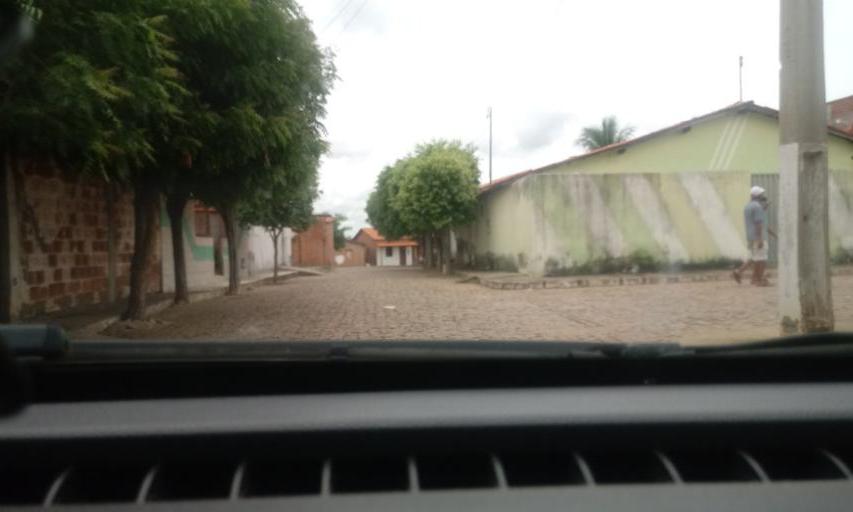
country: BR
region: Bahia
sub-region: Riacho De Santana
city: Riacho de Santana
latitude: -13.9120
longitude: -42.8481
